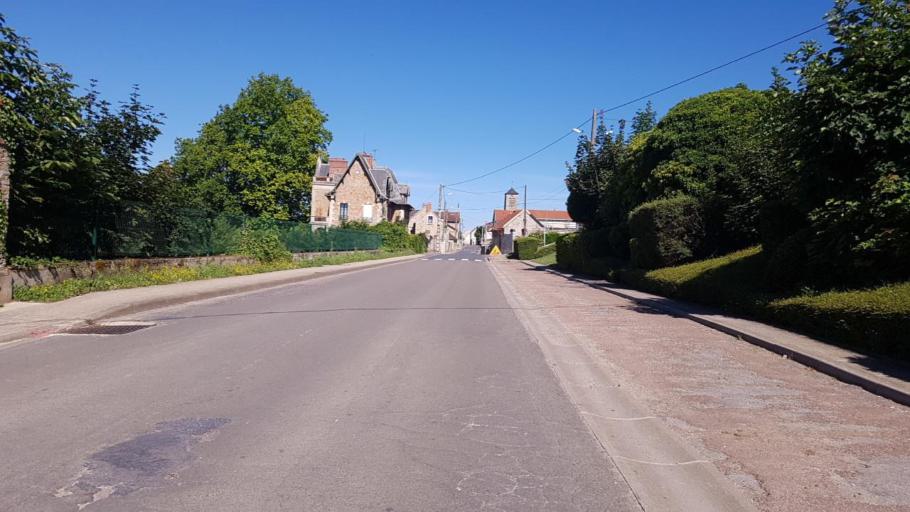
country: FR
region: Picardie
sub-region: Departement de l'Aisne
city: Charly-sur-Marne
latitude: 48.9733
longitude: 3.3109
